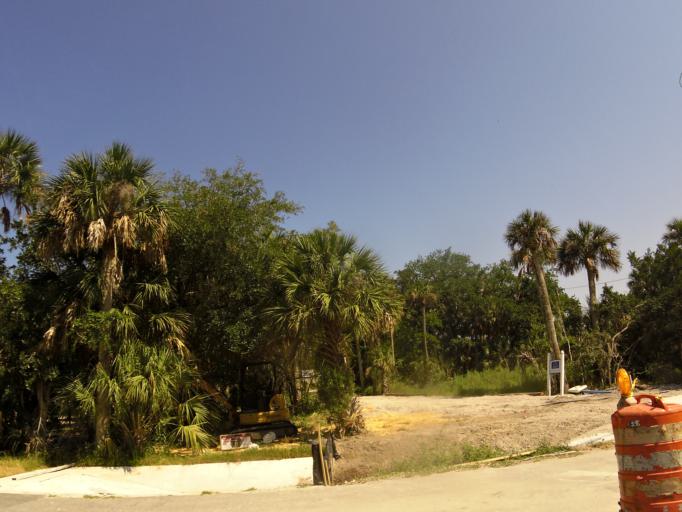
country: US
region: Florida
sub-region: Duval County
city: Atlantic Beach
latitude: 30.4064
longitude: -81.4281
